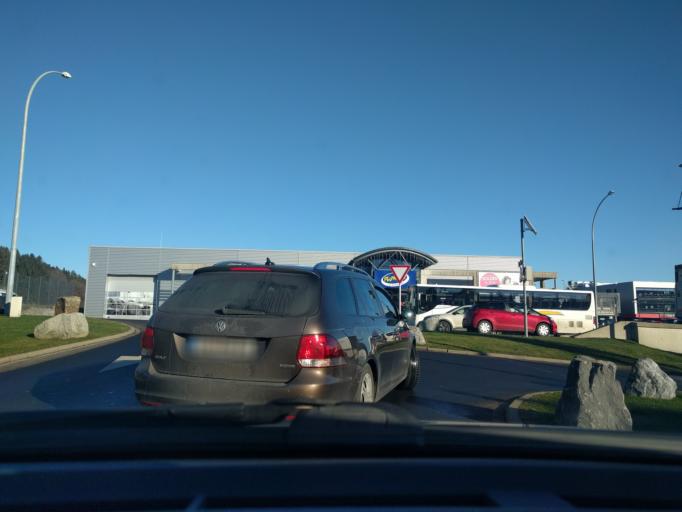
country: LU
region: Diekirch
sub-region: Canton de Clervaux
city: Weiswampach
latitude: 50.1496
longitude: 6.0554
